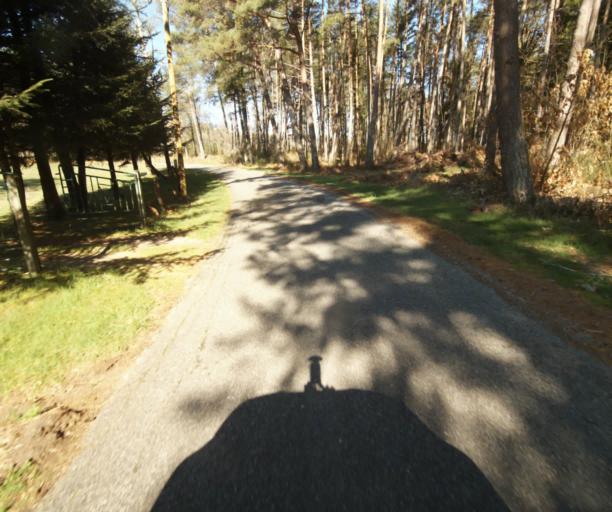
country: FR
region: Limousin
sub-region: Departement de la Correze
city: Correze
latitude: 45.2747
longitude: 1.9335
